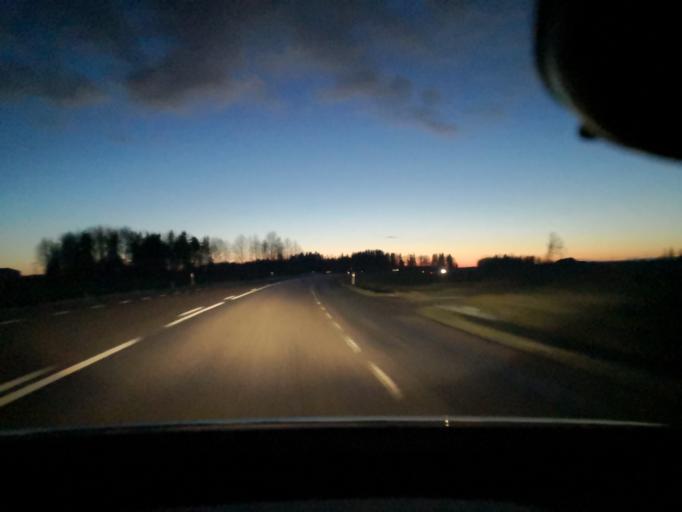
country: SE
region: Vaestmanland
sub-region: Sala Kommun
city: Sala
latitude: 59.9283
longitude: 16.7121
